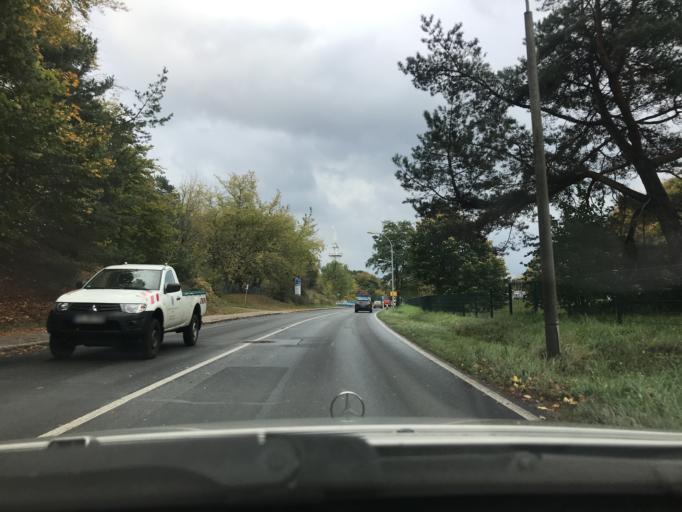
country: DE
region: Mecklenburg-Vorpommern
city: Seebad Heringsdorf
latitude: 53.9478
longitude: 14.1741
